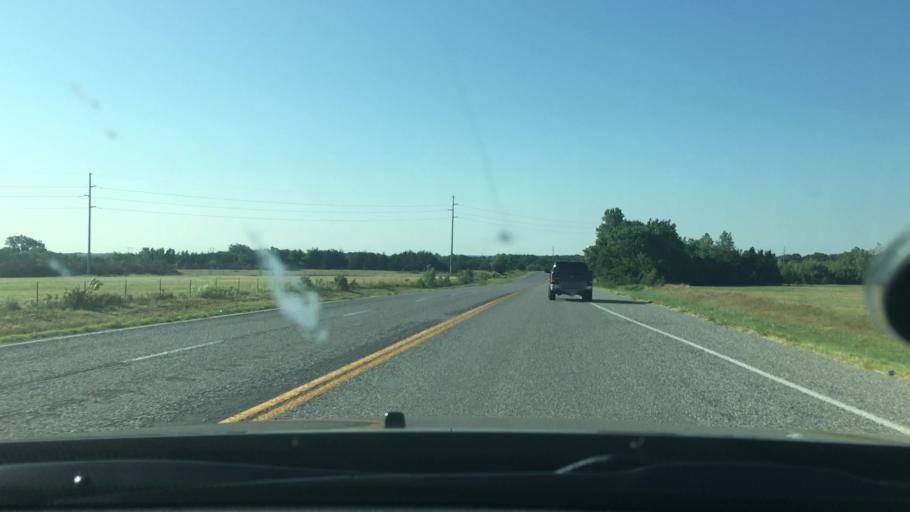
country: US
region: Oklahoma
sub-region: Johnston County
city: Tishomingo
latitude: 34.2765
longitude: -96.7776
